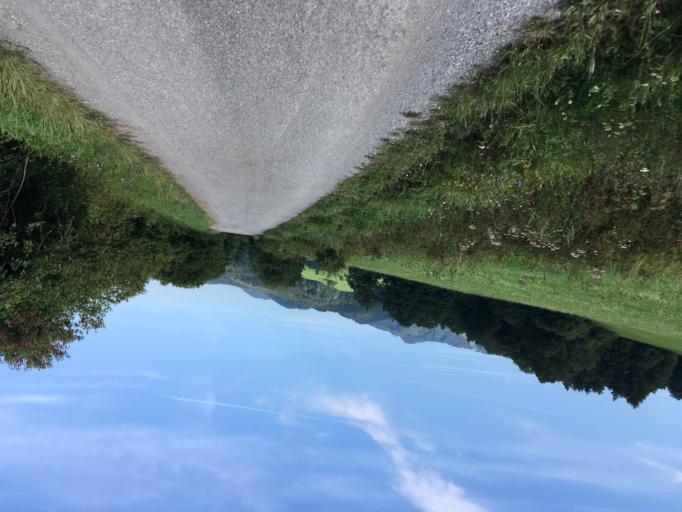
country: SK
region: Trenciansky
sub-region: Okres Povazska Bystrica
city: Povazska Bystrica
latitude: 49.0148
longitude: 18.3733
